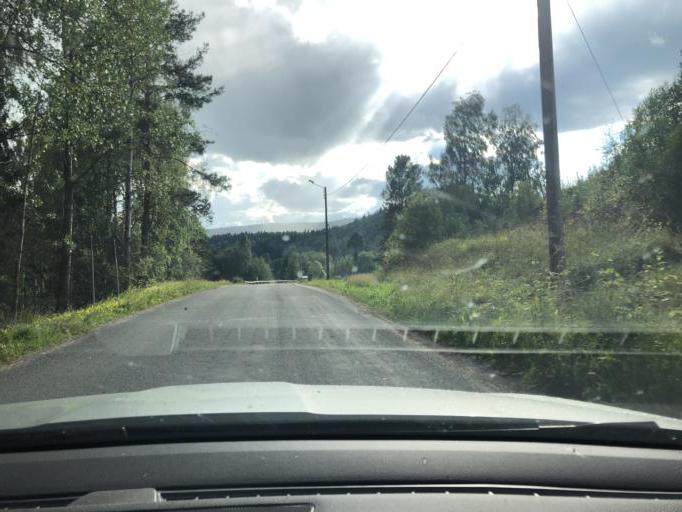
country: SE
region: Vaesternorrland
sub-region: Solleftea Kommun
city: Solleftea
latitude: 63.2471
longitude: 17.1918
